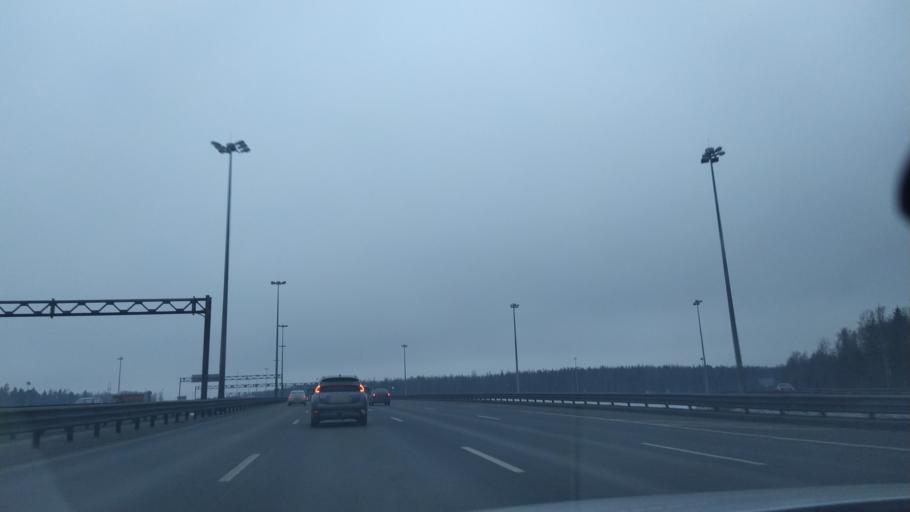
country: RU
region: St.-Petersburg
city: Krasnogvargeisky
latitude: 59.9487
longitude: 30.5427
